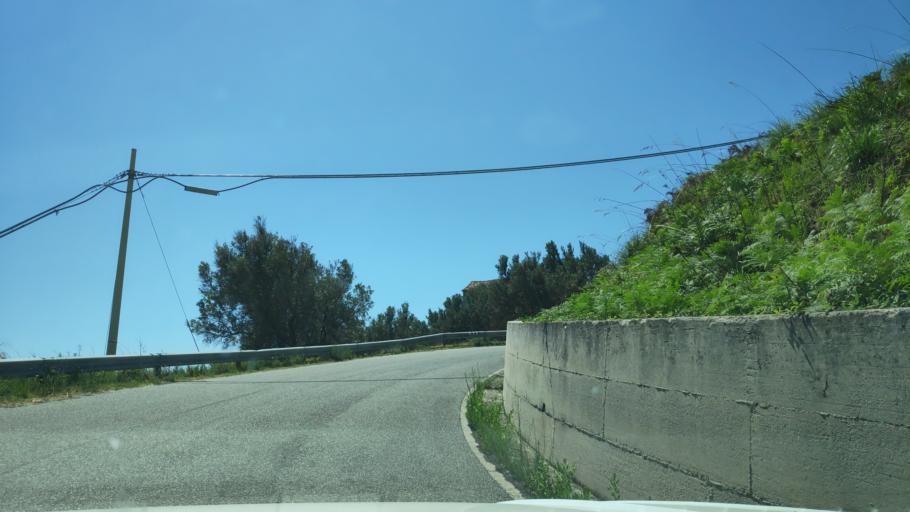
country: IT
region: Calabria
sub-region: Provincia di Catanzaro
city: Gasperina
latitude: 38.7445
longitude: 16.5091
